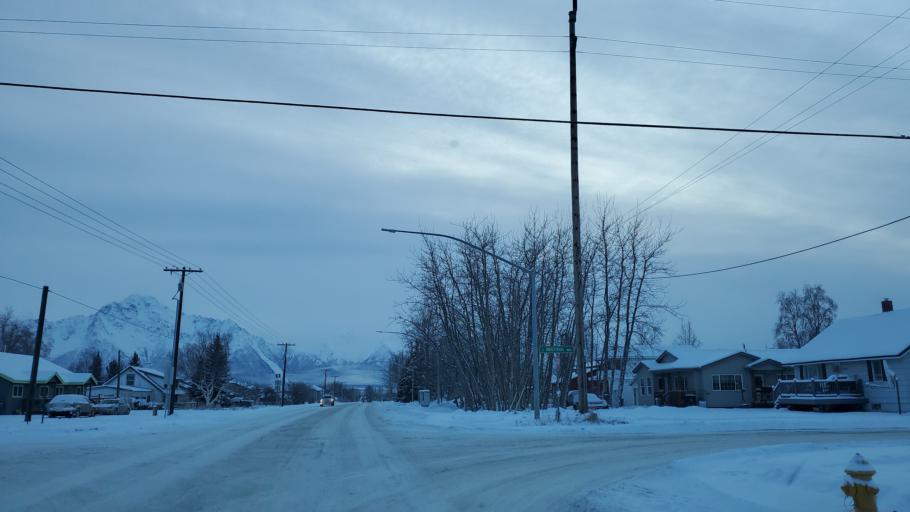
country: US
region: Alaska
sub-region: Matanuska-Susitna Borough
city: Palmer
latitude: 61.5924
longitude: -149.1107
